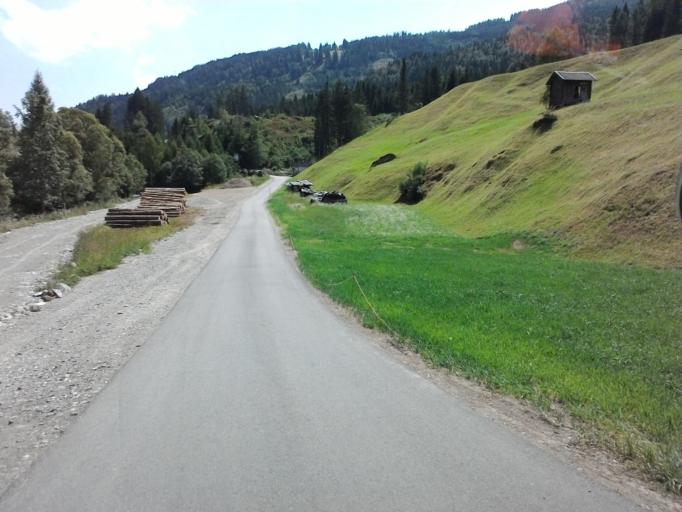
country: AT
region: Tyrol
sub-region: Politischer Bezirk Lienz
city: Untertilliach
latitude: 46.7025
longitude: 12.7403
